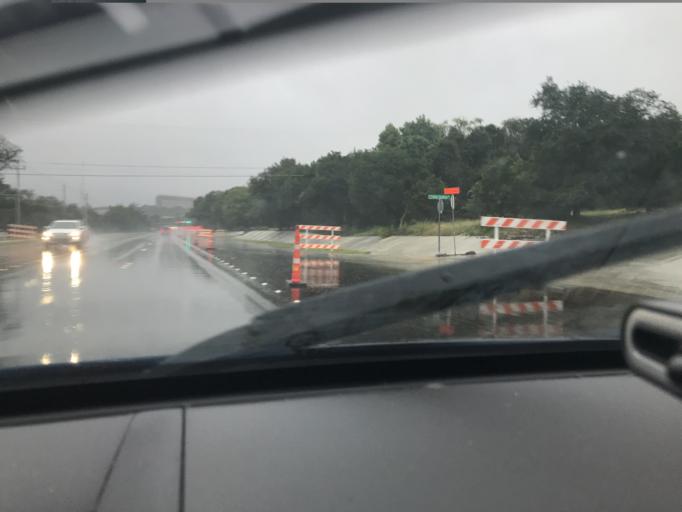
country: US
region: Texas
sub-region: Travis County
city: West Lake Hills
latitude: 30.2905
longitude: -97.8200
